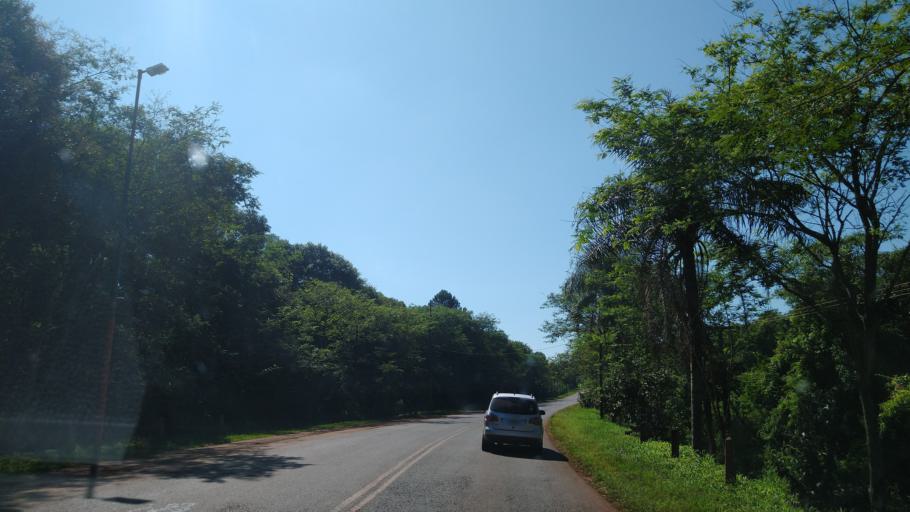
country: AR
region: Misiones
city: Puerto Esperanza
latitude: -26.0190
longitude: -54.5919
